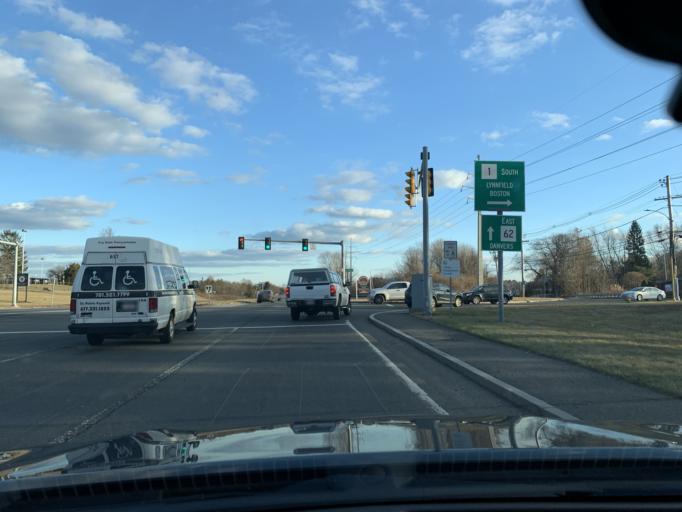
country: US
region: Massachusetts
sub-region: Essex County
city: Danvers
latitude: 42.5860
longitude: -70.9708
